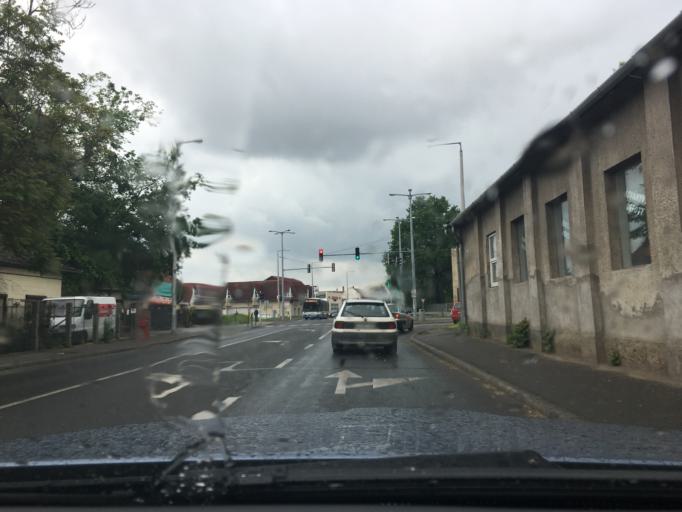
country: HU
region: Hajdu-Bihar
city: Debrecen
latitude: 47.5201
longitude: 21.6588
